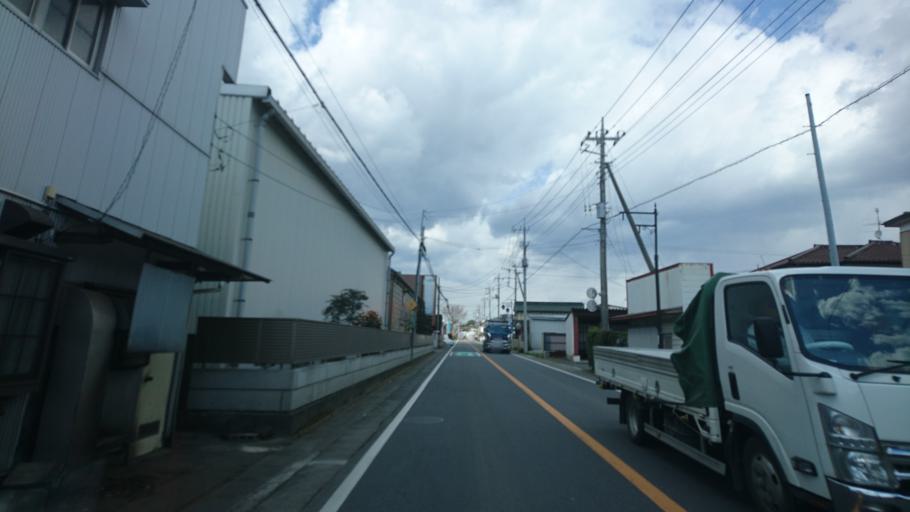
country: JP
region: Ibaraki
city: Shimodate
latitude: 36.2160
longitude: 139.9358
